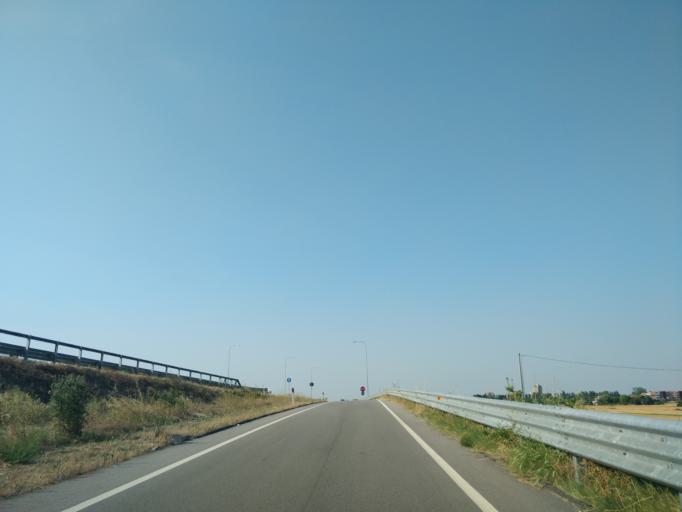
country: IT
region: Emilia-Romagna
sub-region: Provincia di Bologna
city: Progresso
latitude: 44.5628
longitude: 11.3446
